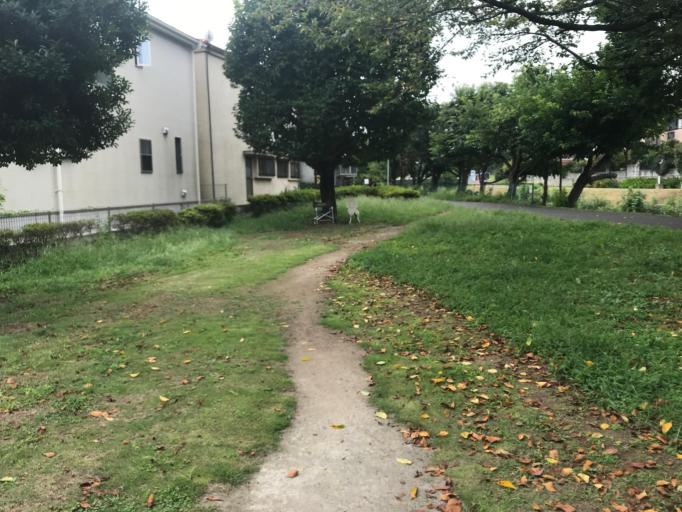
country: JP
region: Tokyo
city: Tanashicho
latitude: 35.7643
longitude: 139.5482
